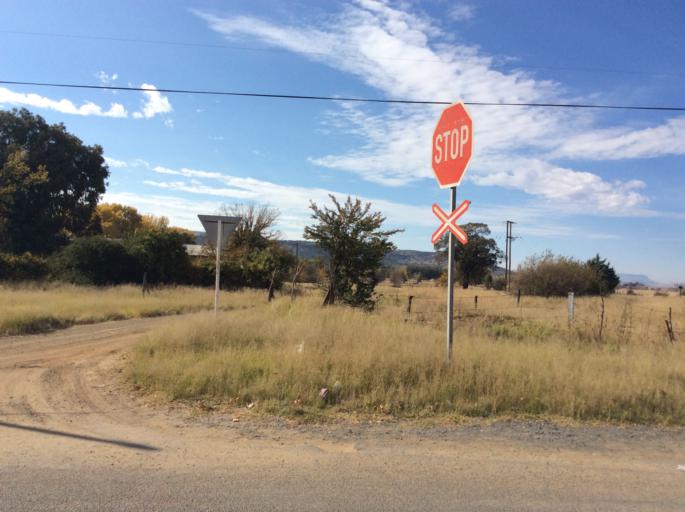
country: LS
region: Mafeteng
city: Mafeteng
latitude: -29.7332
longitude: 27.0309
